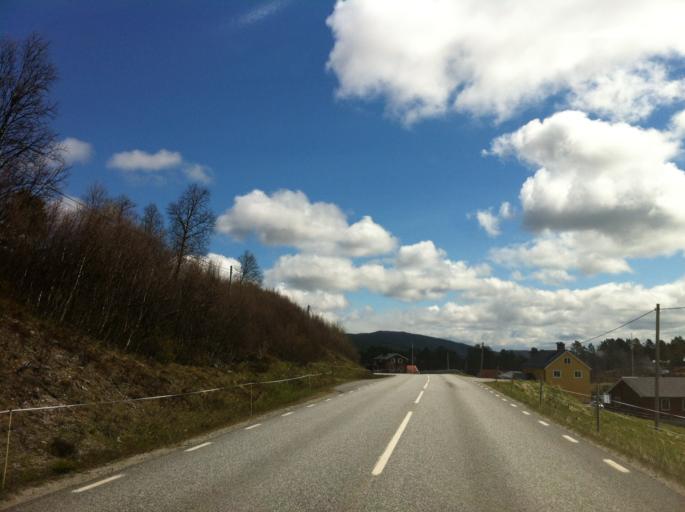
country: NO
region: Sor-Trondelag
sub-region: Tydal
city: Aas
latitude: 62.6220
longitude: 12.4582
